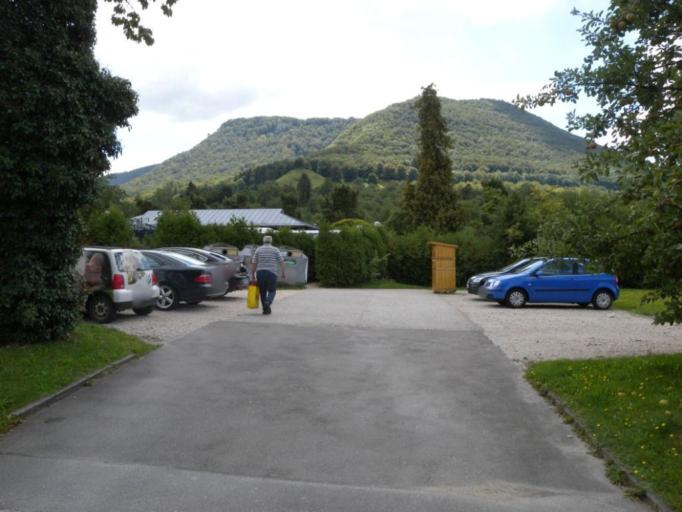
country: DE
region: Baden-Wuerttemberg
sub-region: Tuebingen Region
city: Dettingen an der Erms
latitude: 48.5285
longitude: 9.3443
